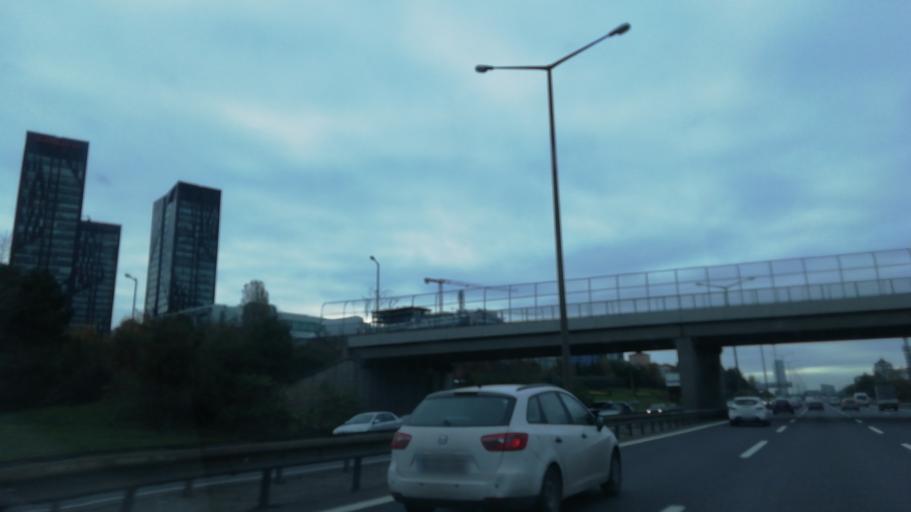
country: TR
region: Istanbul
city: Umraniye
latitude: 41.0290
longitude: 29.1208
